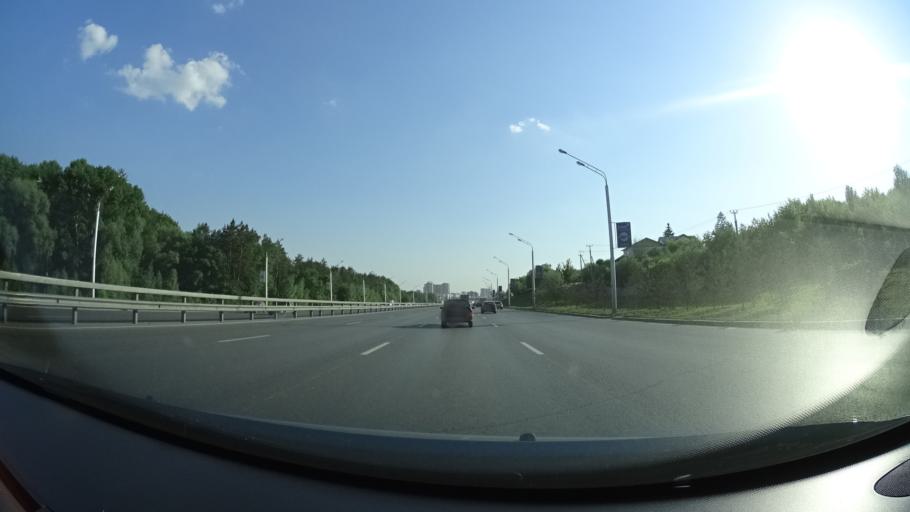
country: RU
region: Bashkortostan
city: Ufa
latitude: 54.7350
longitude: 56.0042
